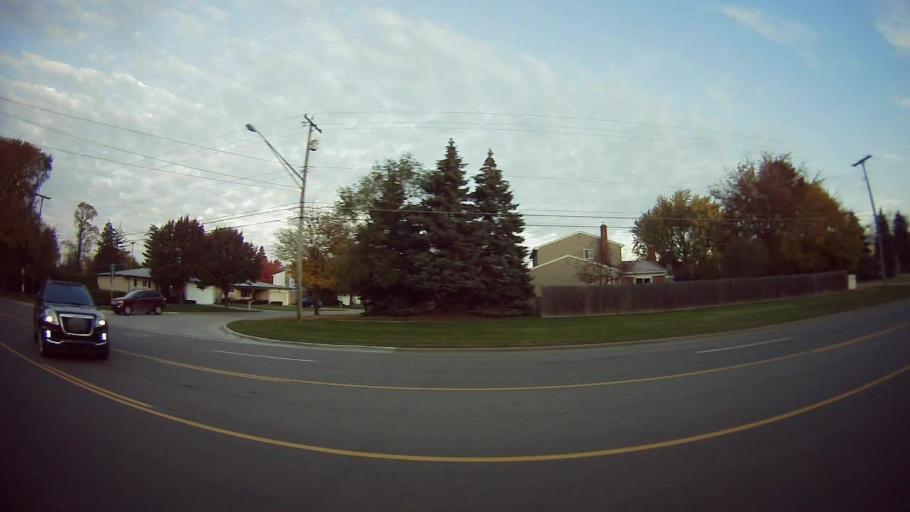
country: US
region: Michigan
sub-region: Macomb County
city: Sterling Heights
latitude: 42.5502
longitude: -83.0747
